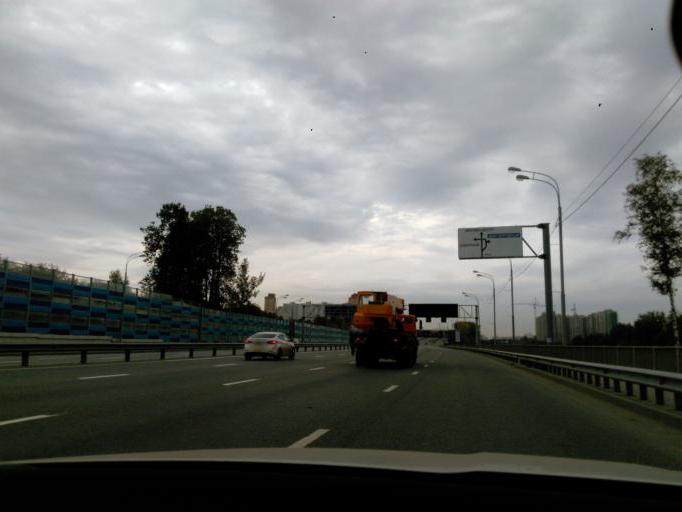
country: RU
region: Moscow
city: Severnyy
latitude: 55.9403
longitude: 37.5444
